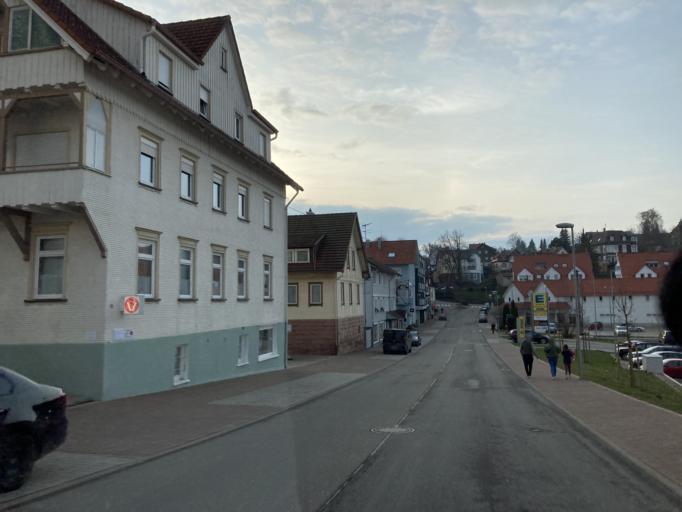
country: DE
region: Baden-Wuerttemberg
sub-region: Karlsruhe Region
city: Schomberg
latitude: 48.7875
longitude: 8.6449
